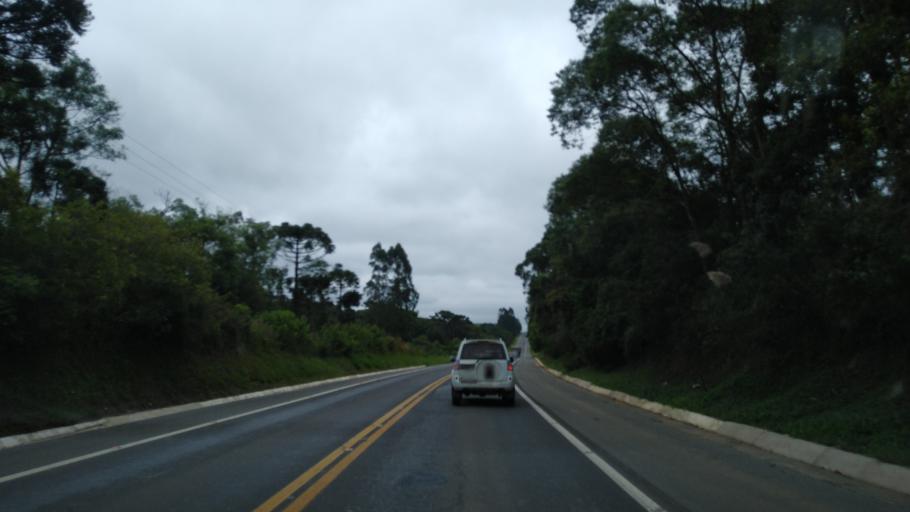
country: BR
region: Santa Catarina
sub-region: Tres Barras
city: Tres Barras
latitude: -26.1833
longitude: -50.2086
